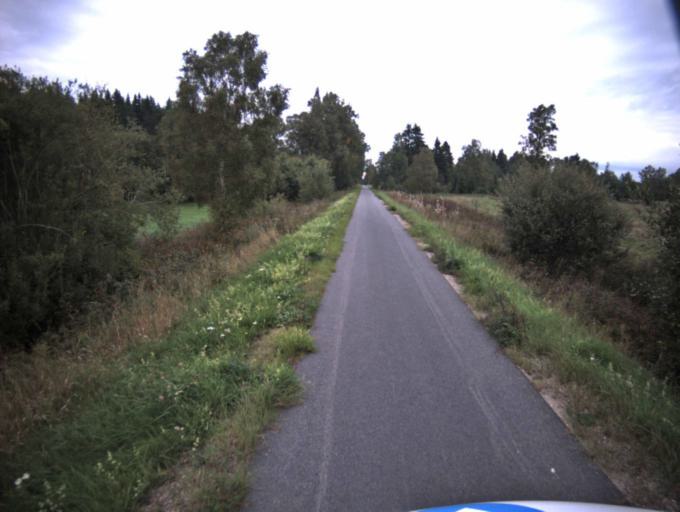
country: SE
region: Vaestra Goetaland
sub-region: Falkopings Kommun
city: Falkoeping
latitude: 58.0040
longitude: 13.5495
